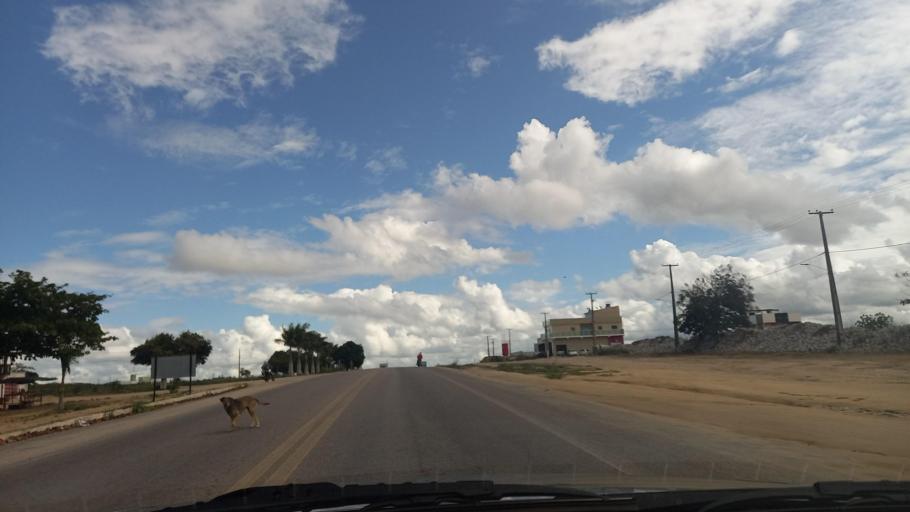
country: BR
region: Pernambuco
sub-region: Lajedo
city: Lajedo
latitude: -8.7136
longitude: -36.4209
